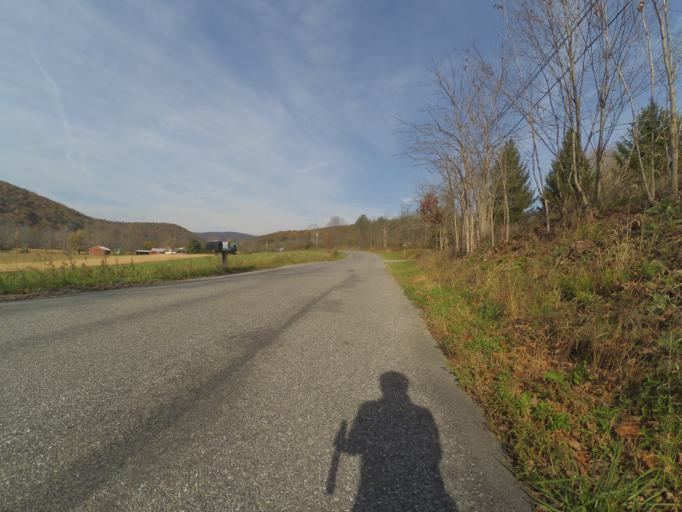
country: US
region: Pennsylvania
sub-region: Centre County
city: Park Forest Village
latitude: 40.8990
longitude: -77.8977
